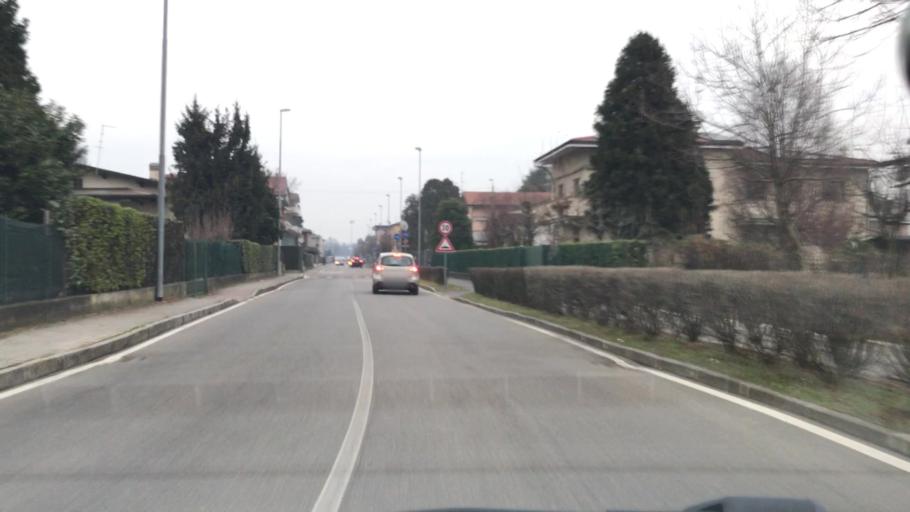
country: IT
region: Lombardy
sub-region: Provincia di Monza e Brianza
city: Seveso
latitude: 45.6472
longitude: 9.1475
